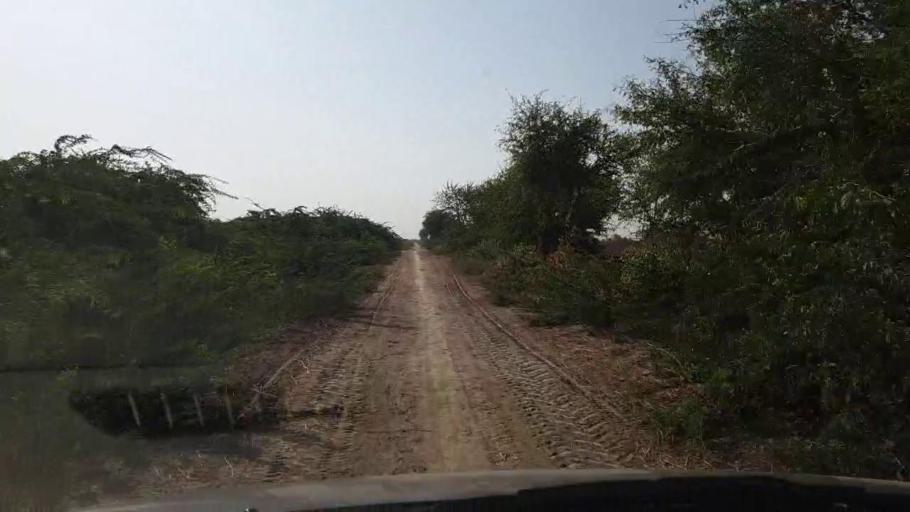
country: PK
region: Sindh
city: Kadhan
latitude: 24.5983
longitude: 69.0752
